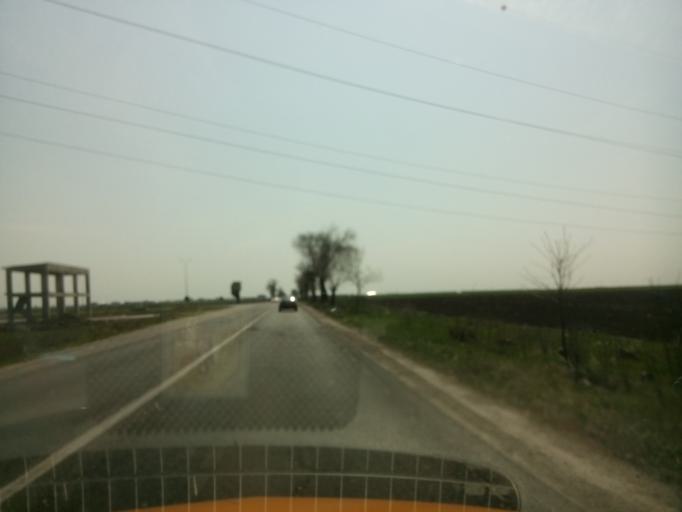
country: RO
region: Ilfov
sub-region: Comuna Glina
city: Glina
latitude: 44.3496
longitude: 26.2185
